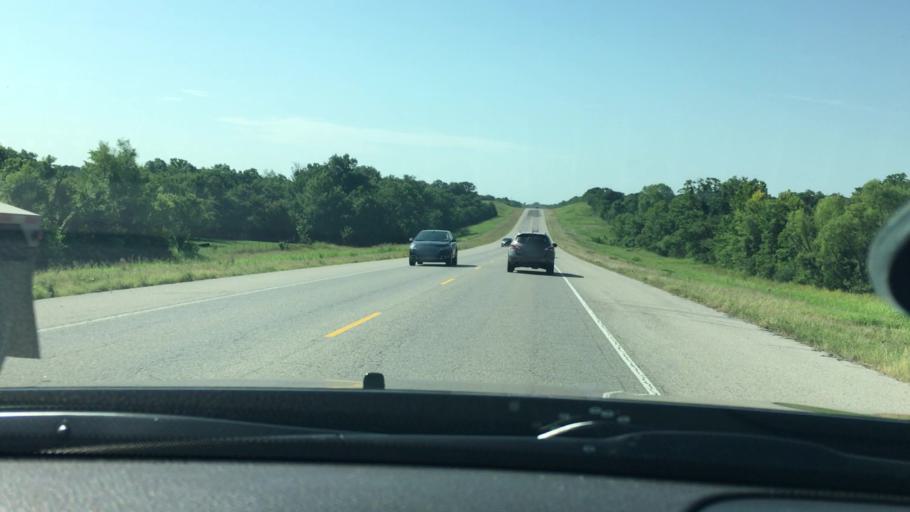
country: US
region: Oklahoma
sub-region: Pontotoc County
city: Ada
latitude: 34.6644
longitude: -96.5644
